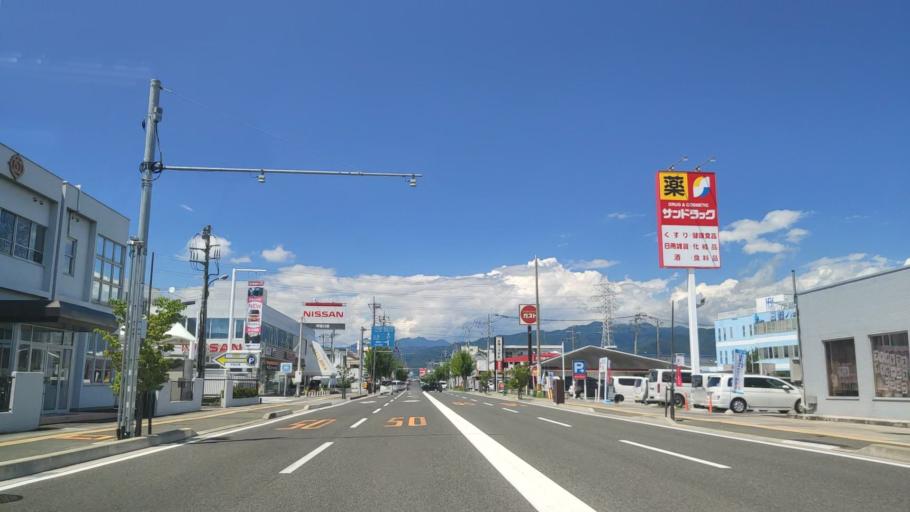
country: JP
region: Yamanashi
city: Kofu-shi
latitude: 35.6249
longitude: 138.5719
